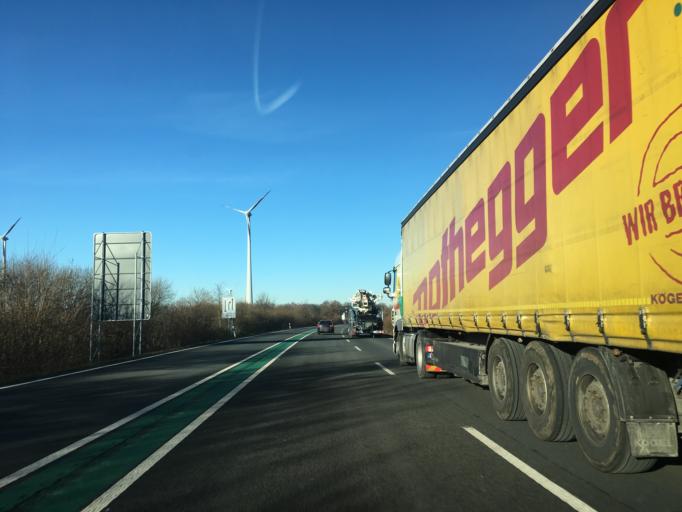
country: DE
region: North Rhine-Westphalia
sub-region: Regierungsbezirk Munster
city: Altenberge
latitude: 52.0779
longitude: 7.4225
